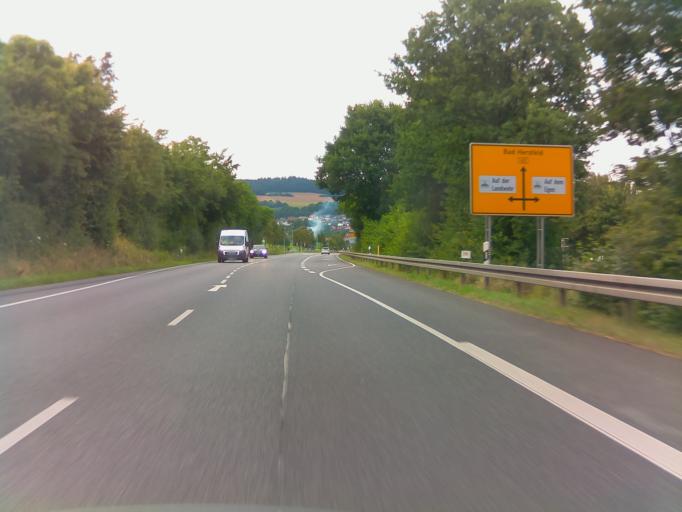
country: DE
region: Hesse
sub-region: Regierungsbezirk Kassel
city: Niederaula
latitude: 50.7882
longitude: 9.5939
